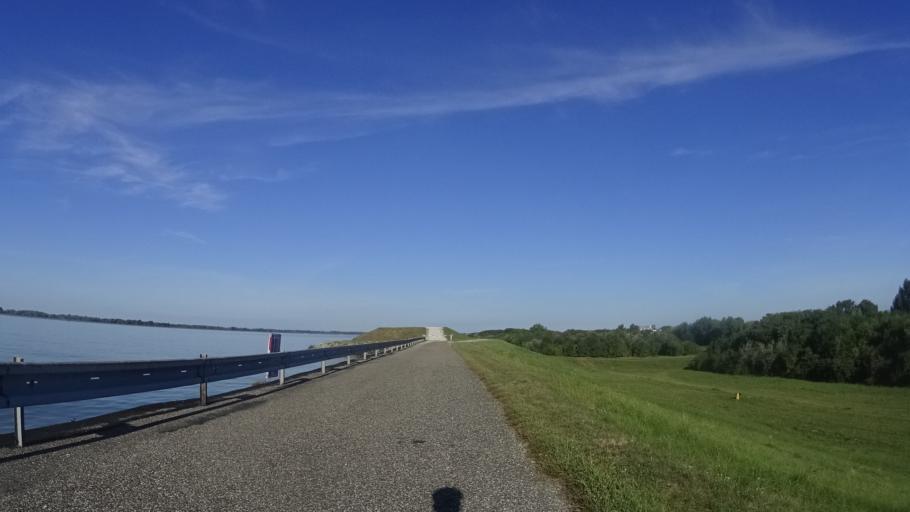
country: SK
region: Trnavsky
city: Samorin
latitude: 48.0065
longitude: 17.3215
